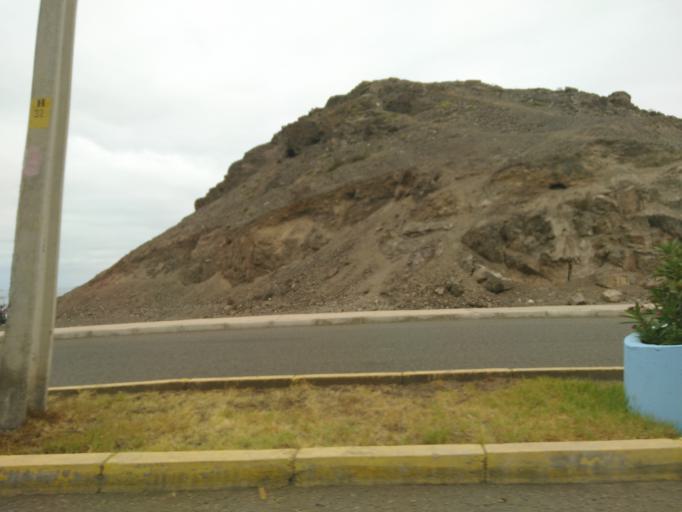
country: CL
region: Antofagasta
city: Taltal
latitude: -25.4043
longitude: -70.4803
